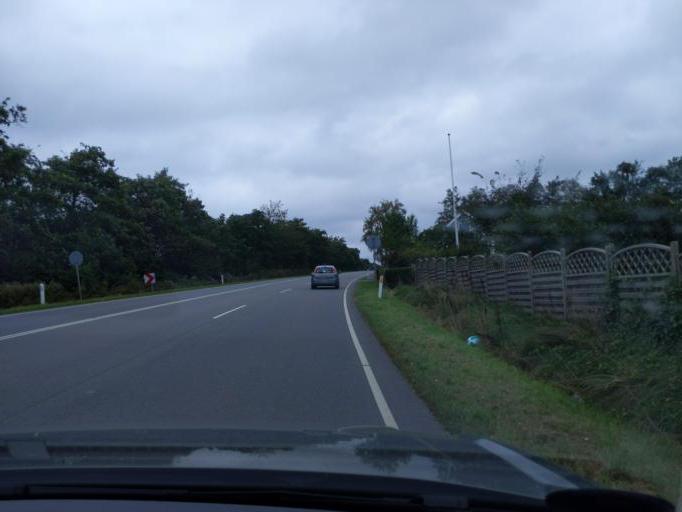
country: DK
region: North Denmark
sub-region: Mariagerfjord Kommune
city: Hobro
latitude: 56.5710
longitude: 9.8184
